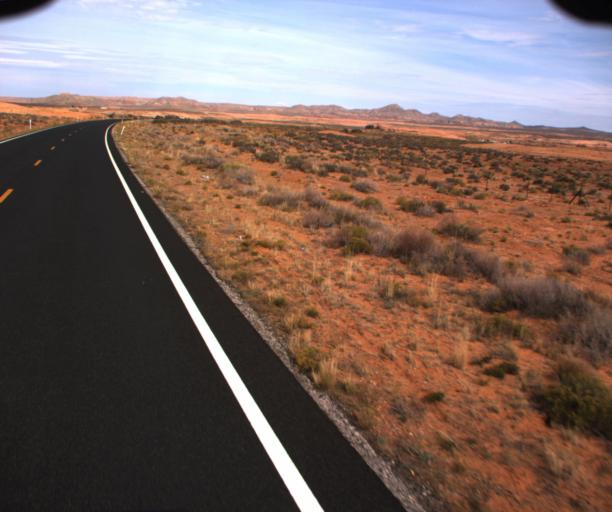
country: US
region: Arizona
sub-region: Apache County
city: Many Farms
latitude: 36.9124
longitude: -109.6230
